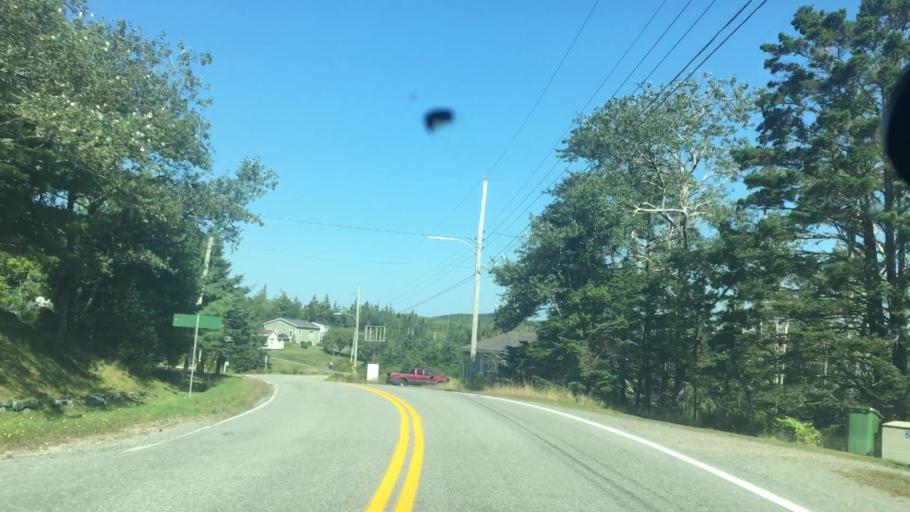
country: CA
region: Nova Scotia
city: New Glasgow
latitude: 44.9140
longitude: -62.3841
